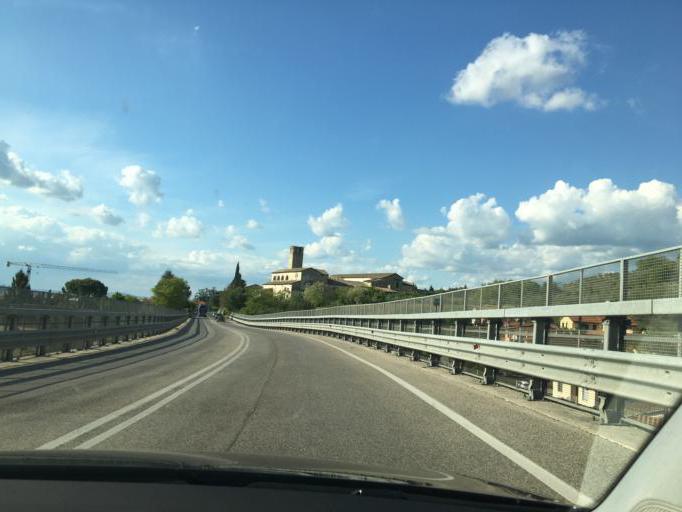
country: IT
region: Umbria
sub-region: Provincia di Perugia
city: Spoleto
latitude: 42.7373
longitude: 12.7420
